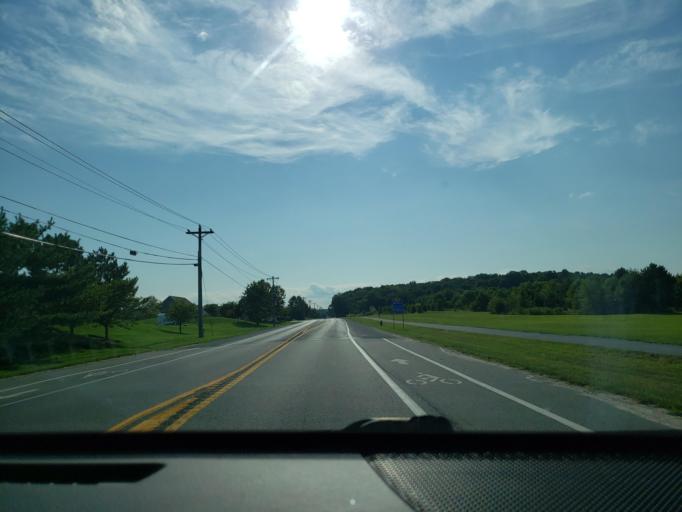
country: US
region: Delaware
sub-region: Sussex County
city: Milton
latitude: 38.7575
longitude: -75.2347
